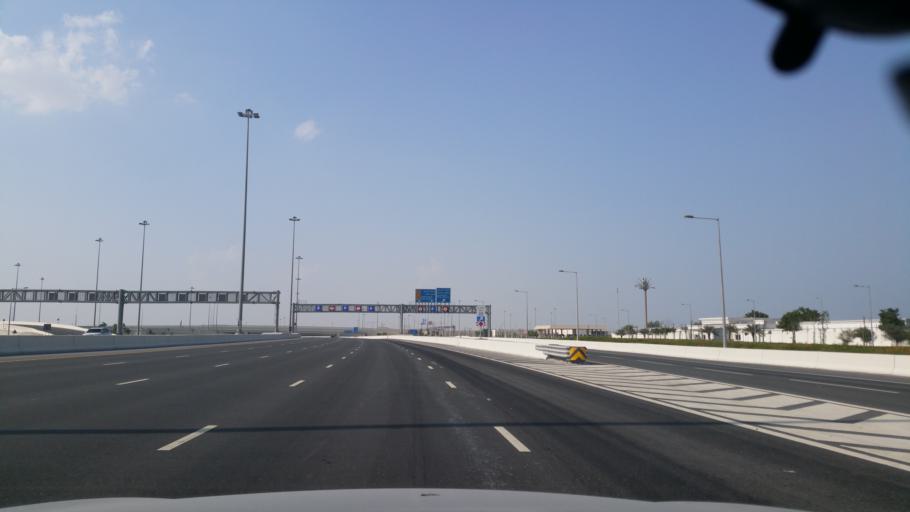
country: QA
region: Baladiyat Umm Salal
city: Umm Salal Muhammad
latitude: 25.3879
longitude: 51.4997
